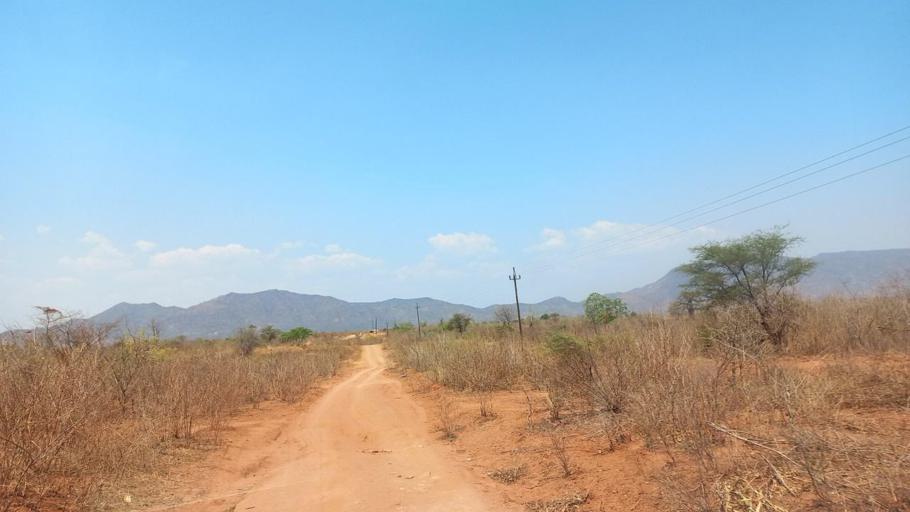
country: ZM
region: Lusaka
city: Luangwa
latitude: -15.5939
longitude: 30.3847
